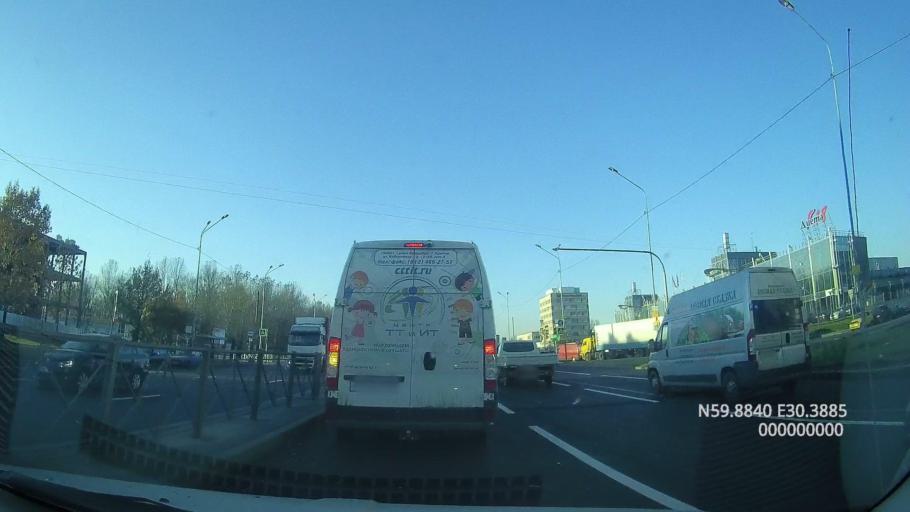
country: RU
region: St.-Petersburg
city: Kupchino
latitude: 59.8841
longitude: 30.3884
